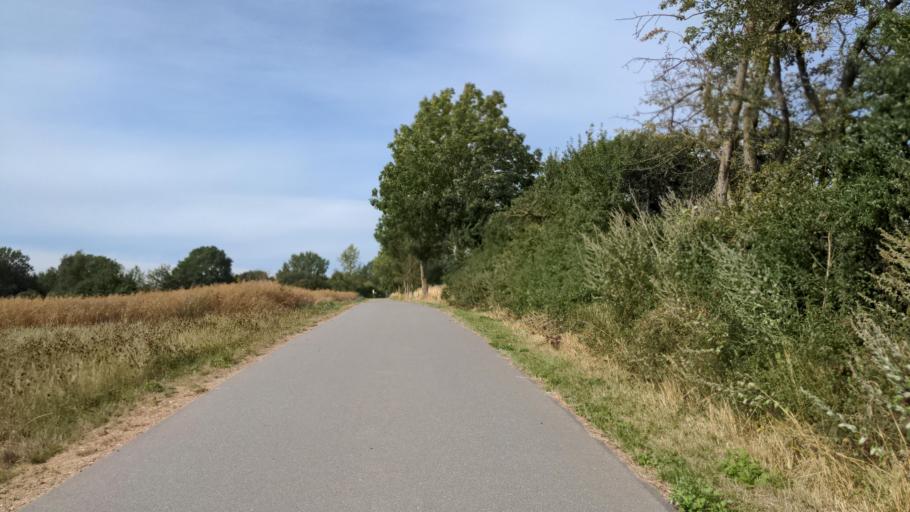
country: DE
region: Mecklenburg-Vorpommern
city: Kalkhorst
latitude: 54.0078
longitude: 11.0789
